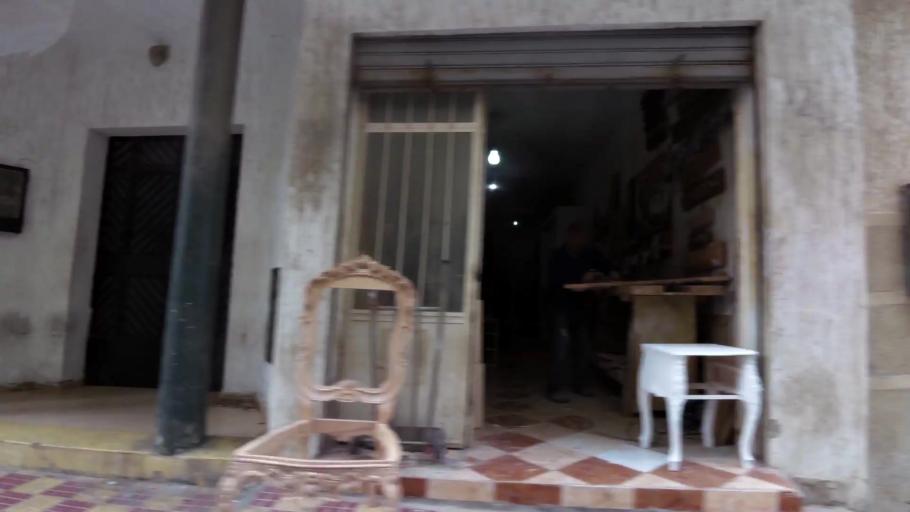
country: MA
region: Tanger-Tetouan
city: Tetouan
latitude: 35.5768
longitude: -5.3596
